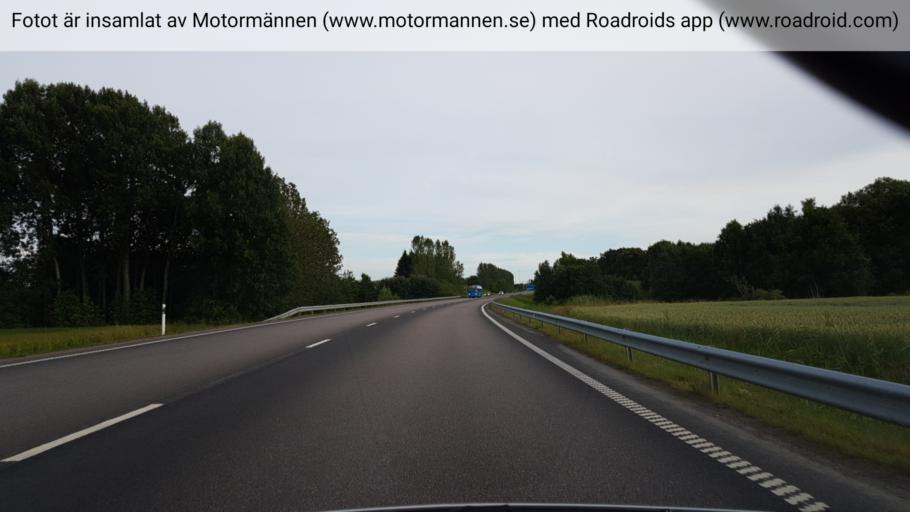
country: SE
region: Vaestra Goetaland
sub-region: Skara Kommun
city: Skara
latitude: 58.3884
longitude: 13.4098
